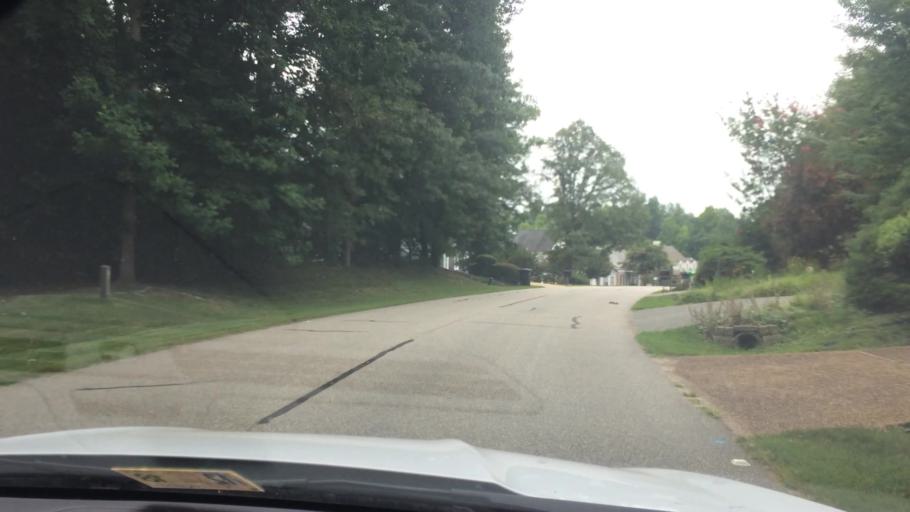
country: US
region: Virginia
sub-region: James City County
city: Williamsburg
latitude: 37.3044
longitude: -76.7701
